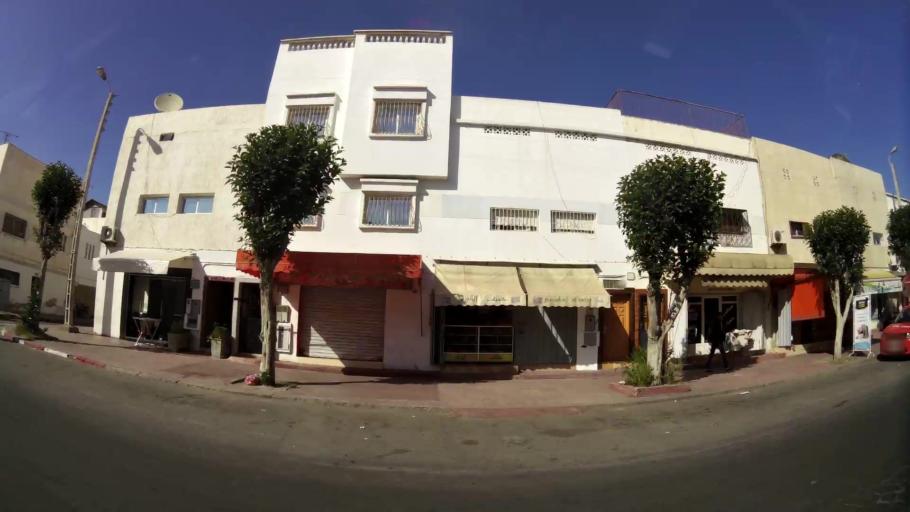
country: MA
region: Oued ed Dahab-Lagouira
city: Dakhla
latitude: 30.4228
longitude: -9.5617
